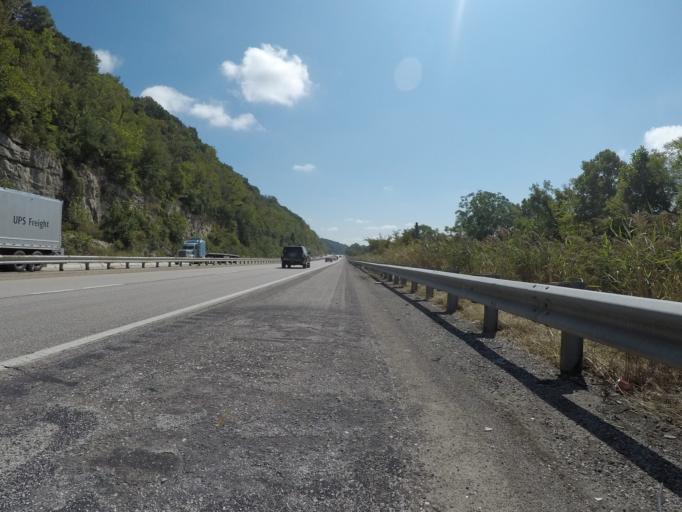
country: US
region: Kentucky
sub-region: Boyd County
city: Ashland
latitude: 38.4774
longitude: -82.6170
